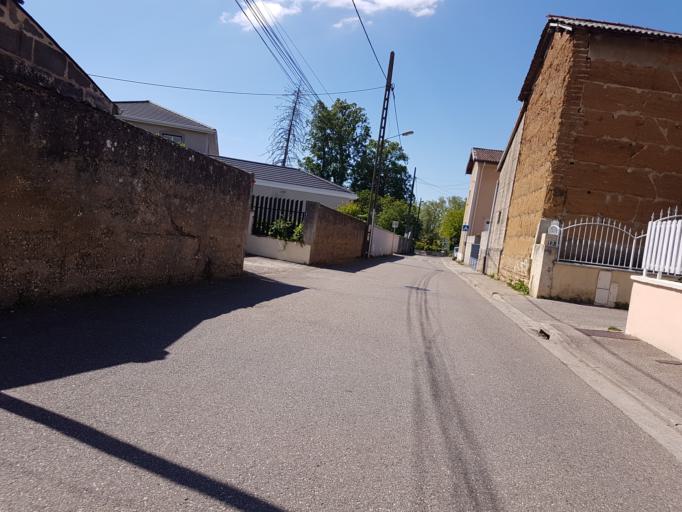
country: FR
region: Rhone-Alpes
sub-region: Departement du Rhone
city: Jonage
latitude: 45.7971
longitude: 5.0427
